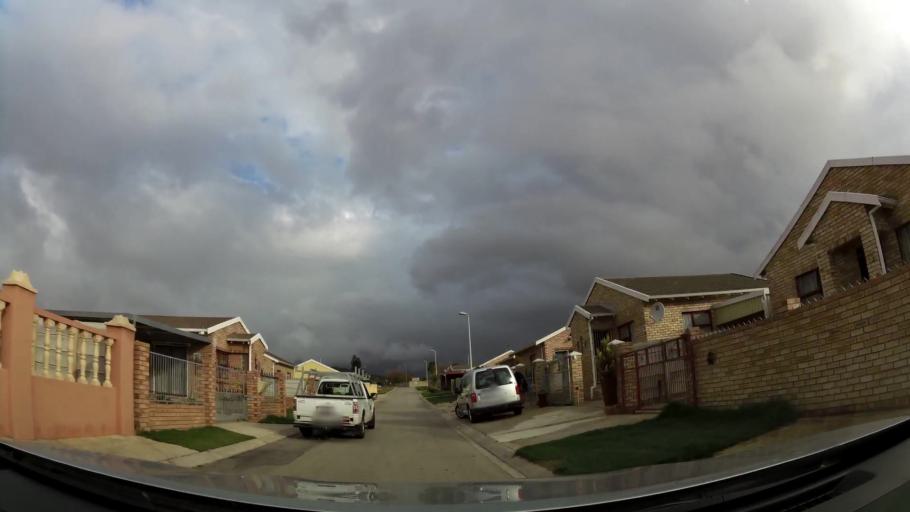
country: ZA
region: Eastern Cape
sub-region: Nelson Mandela Bay Metropolitan Municipality
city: Uitenhage
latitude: -33.7990
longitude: 25.4555
